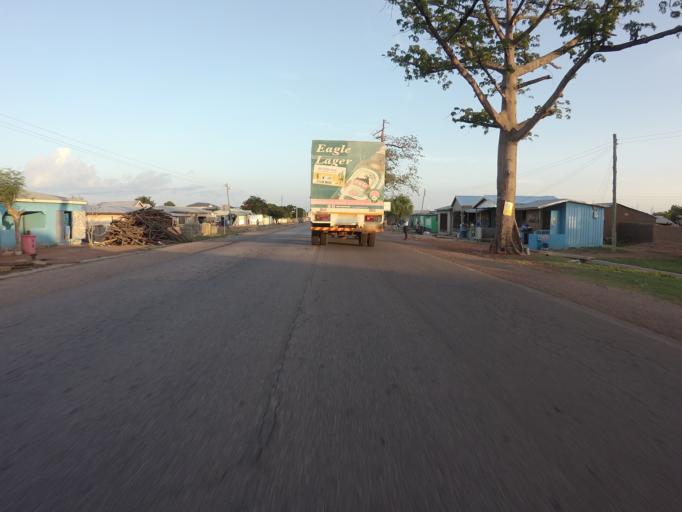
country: GH
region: Upper East
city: Navrongo
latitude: 10.9651
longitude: -1.1007
